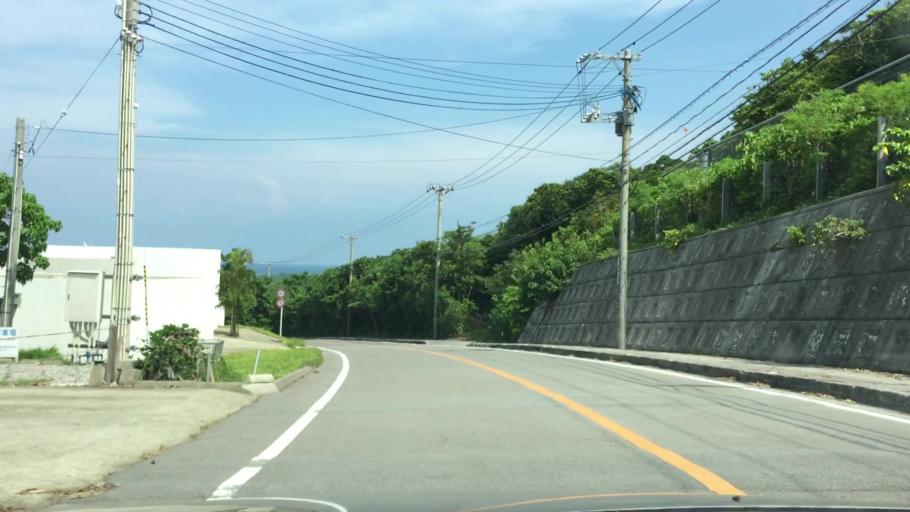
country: JP
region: Okinawa
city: Ishigaki
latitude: 24.5151
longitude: 124.2628
